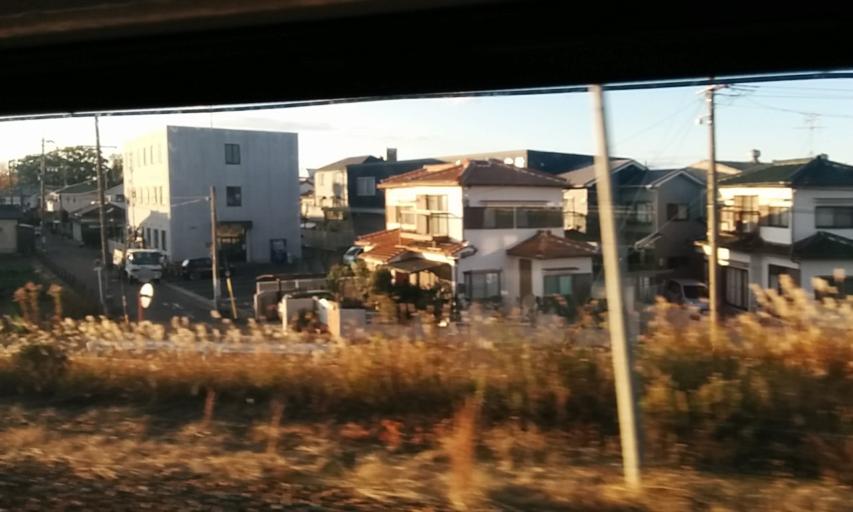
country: JP
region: Aichi
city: Kasugai
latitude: 35.2467
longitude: 136.9920
